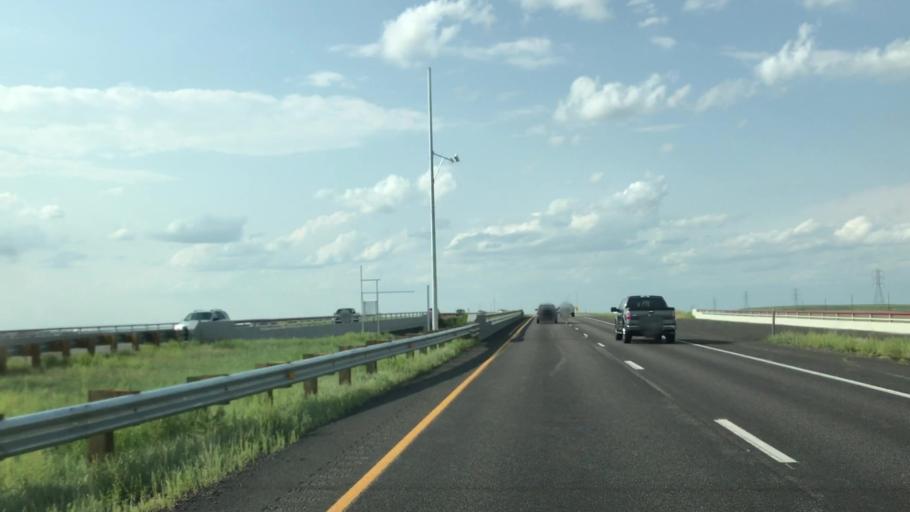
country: US
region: Colorado
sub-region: Arapahoe County
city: Dove Valley
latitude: 39.6377
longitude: -104.7190
